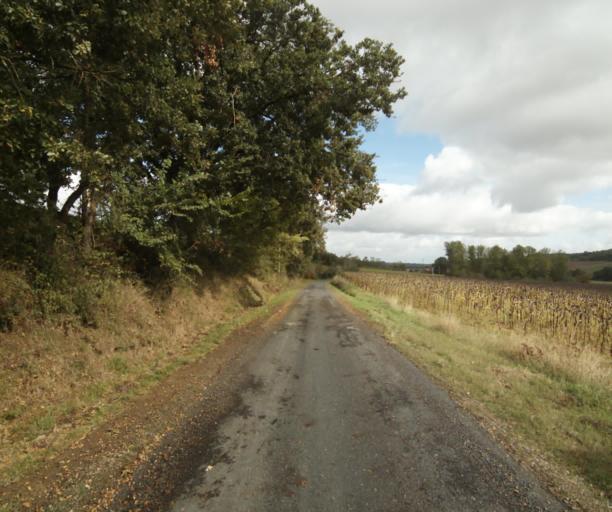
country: FR
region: Midi-Pyrenees
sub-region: Departement du Tarn-et-Garonne
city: Beaumont-de-Lomagne
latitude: 43.8651
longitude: 1.1050
